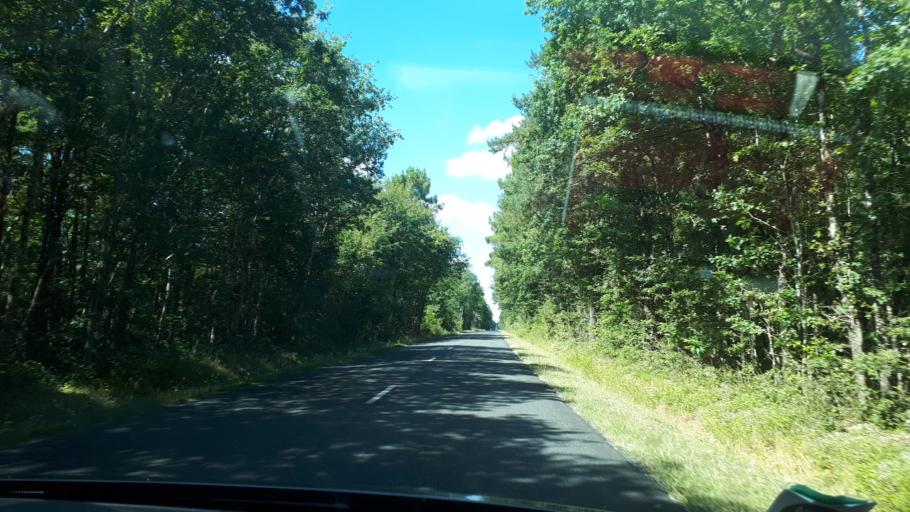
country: FR
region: Centre
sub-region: Departement du Loir-et-Cher
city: Neung-sur-Beuvron
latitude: 47.5339
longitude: 1.7470
